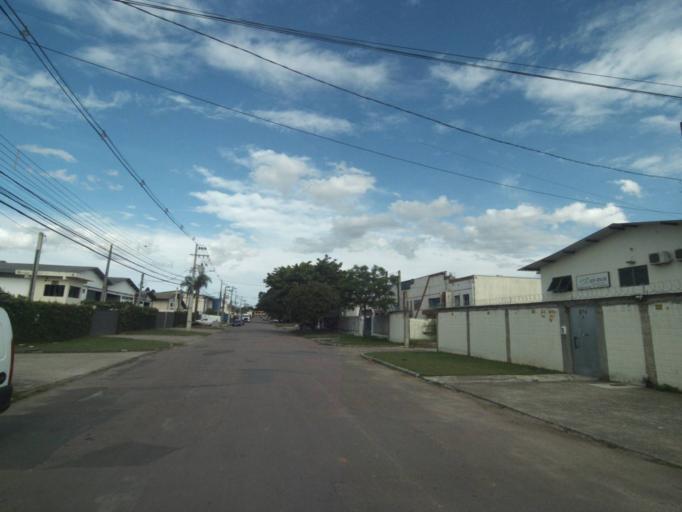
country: BR
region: Parana
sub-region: Curitiba
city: Curitiba
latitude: -25.4979
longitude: -49.3327
